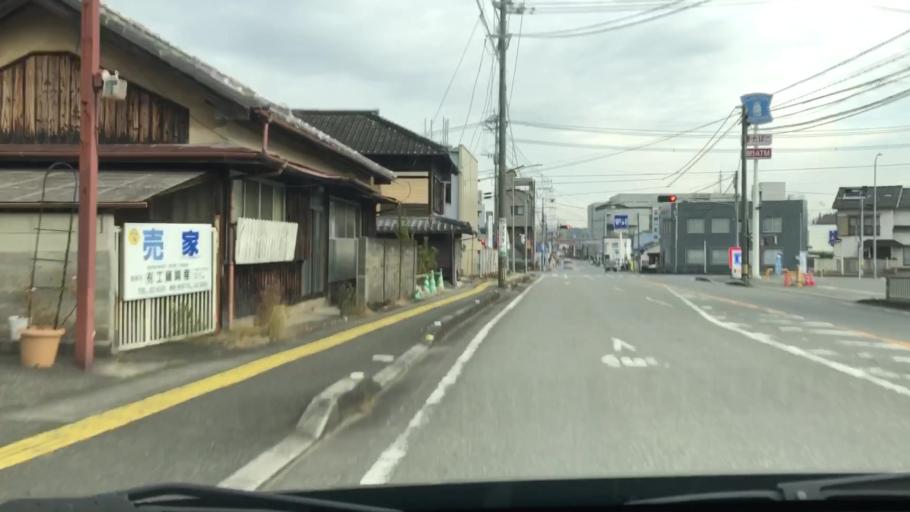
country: JP
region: Oita
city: Takedamachi
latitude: 32.9755
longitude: 131.5814
